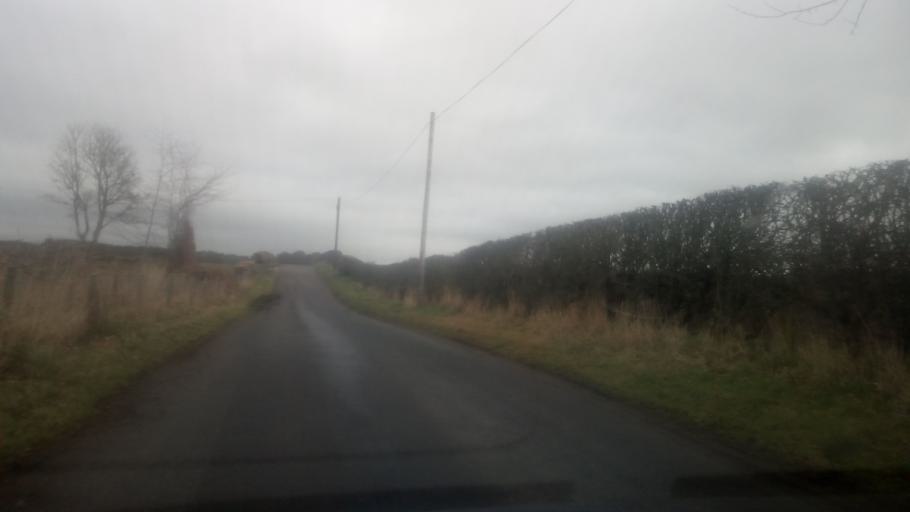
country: GB
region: Scotland
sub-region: The Scottish Borders
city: Jedburgh
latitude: 55.5355
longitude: -2.4981
